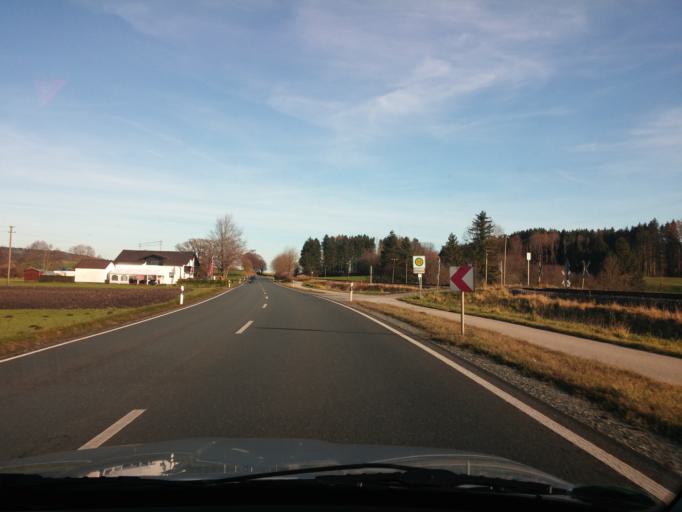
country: DE
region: Bavaria
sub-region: Upper Bavaria
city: Steinhoring
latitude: 48.0836
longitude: 12.0462
